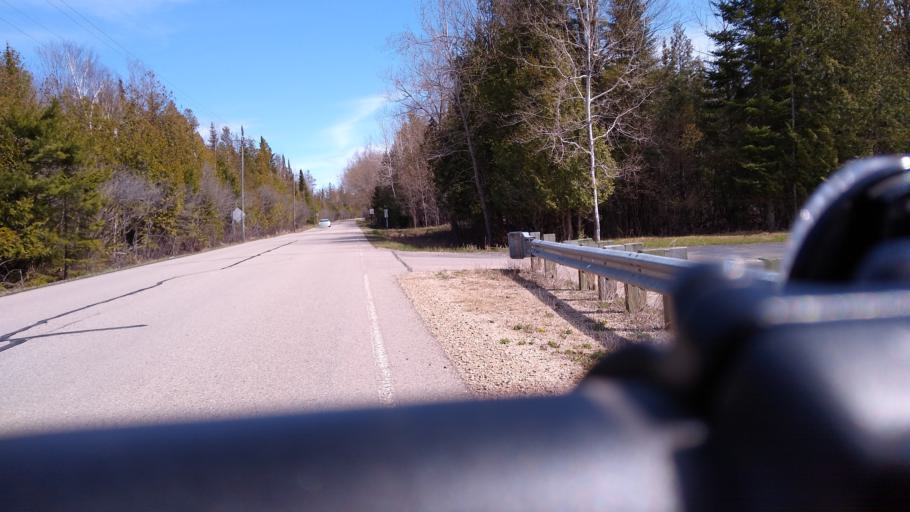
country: US
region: Michigan
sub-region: Delta County
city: Escanaba
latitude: 45.6857
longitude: -87.1507
